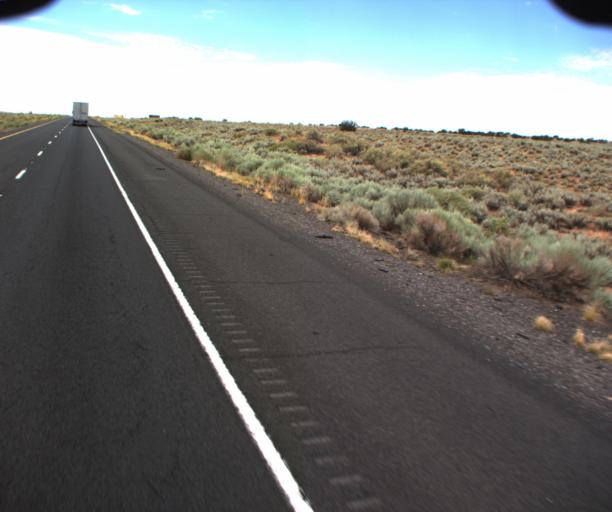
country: US
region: Arizona
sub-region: Apache County
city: Houck
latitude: 35.1443
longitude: -109.5174
